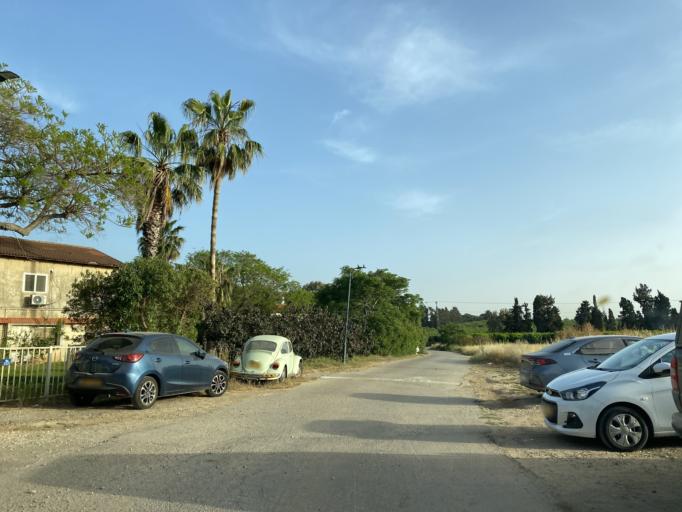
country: IL
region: Tel Aviv
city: Herzliyya
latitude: 32.1563
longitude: 34.8289
